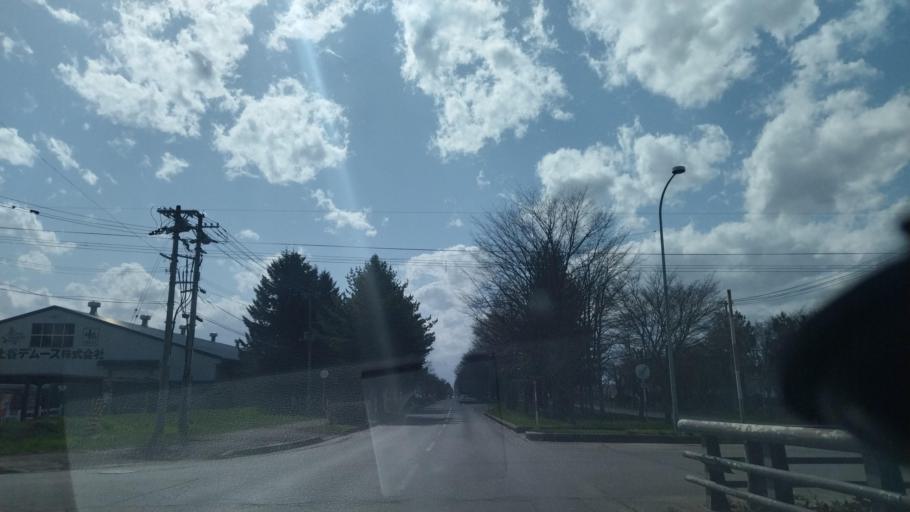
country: JP
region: Hokkaido
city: Obihiro
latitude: 42.9300
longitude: 143.1407
